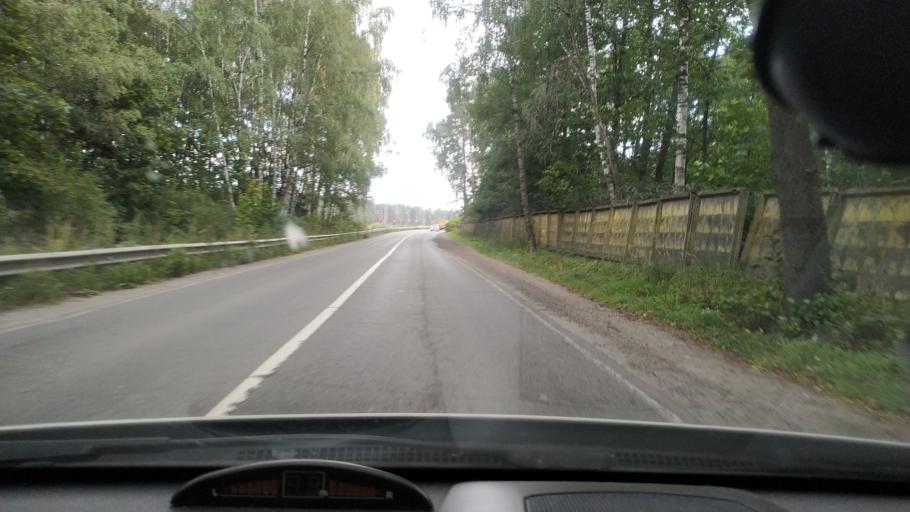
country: RU
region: Moskovskaya
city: Chornaya
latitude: 55.7750
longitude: 38.0502
